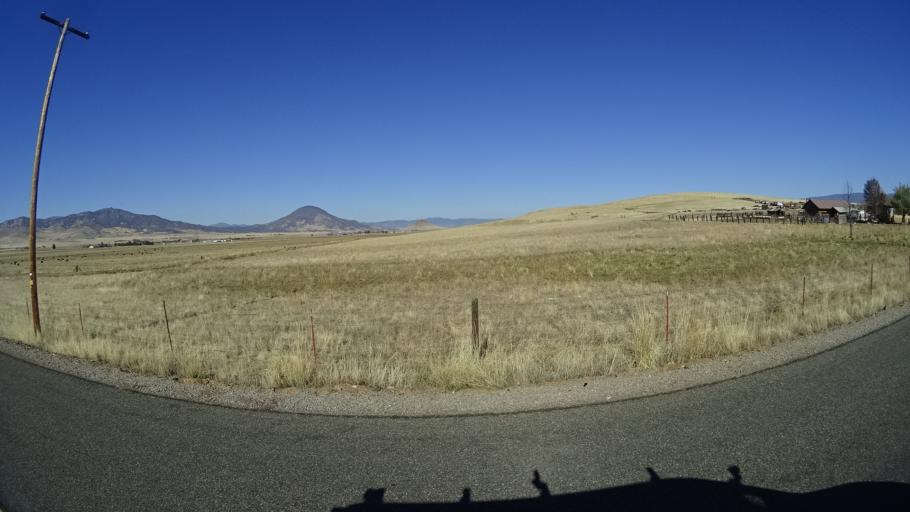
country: US
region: California
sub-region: Siskiyou County
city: Montague
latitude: 41.7558
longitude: -122.4675
